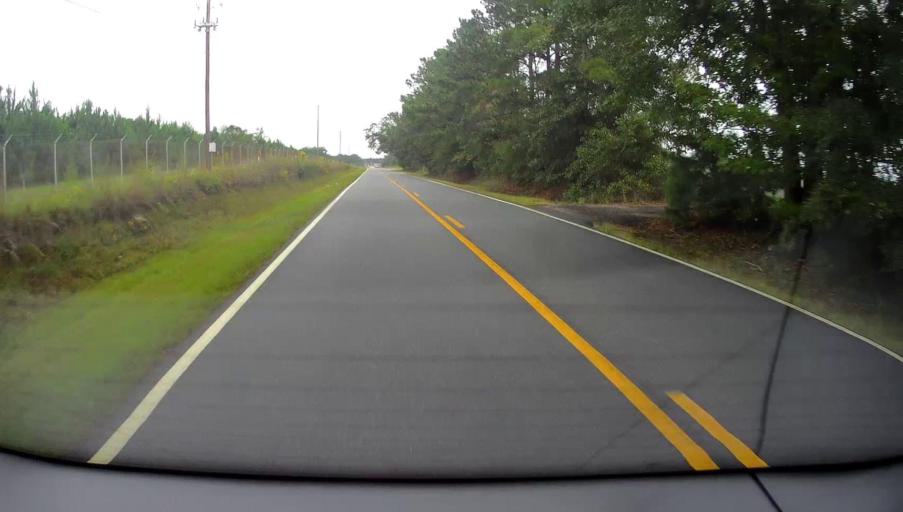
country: US
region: Georgia
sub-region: Houston County
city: Centerville
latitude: 32.6514
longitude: -83.7208
